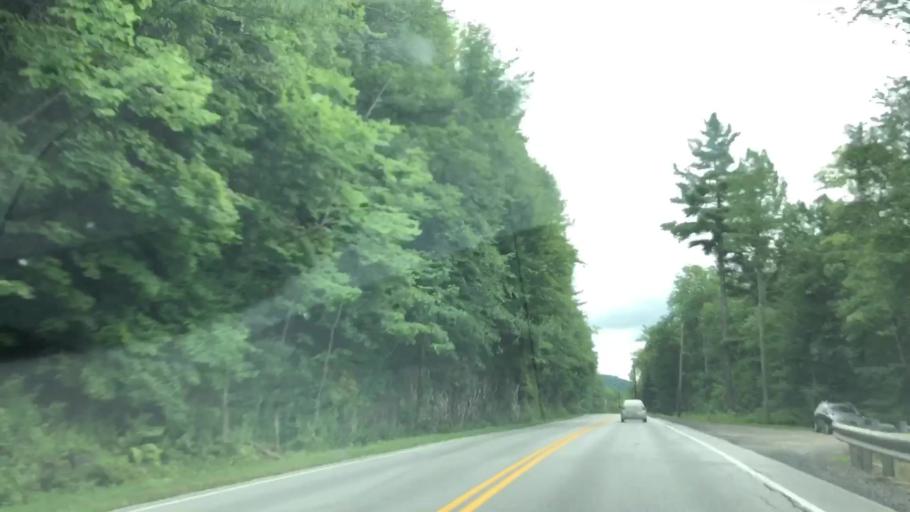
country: US
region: Vermont
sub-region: Rutland County
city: Rutland
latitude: 43.7499
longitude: -72.8210
